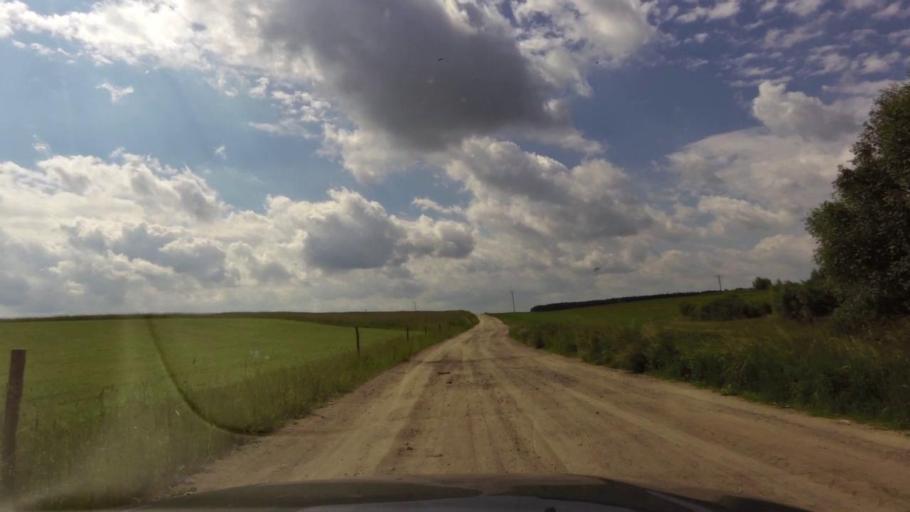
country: PL
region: West Pomeranian Voivodeship
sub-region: Powiat pyrzycki
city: Lipiany
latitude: 52.9643
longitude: 14.9314
